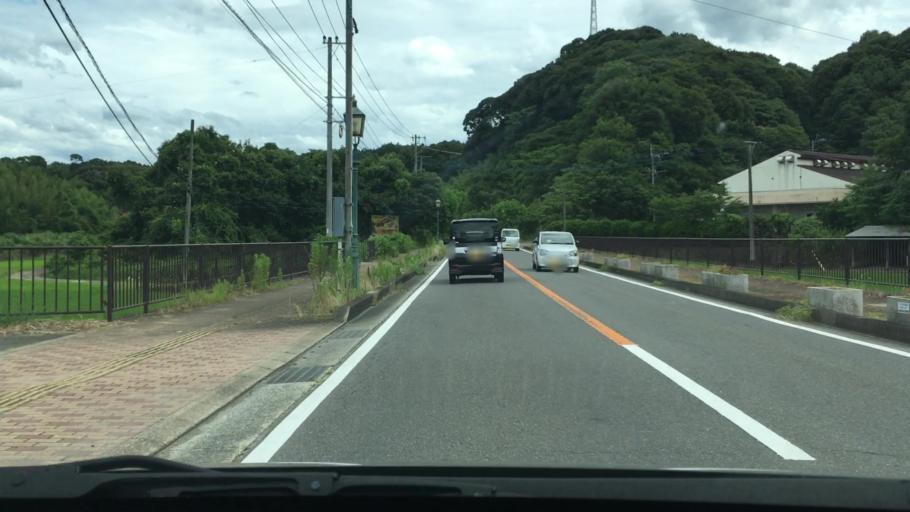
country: JP
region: Nagasaki
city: Togitsu
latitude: 32.9881
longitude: 129.7667
